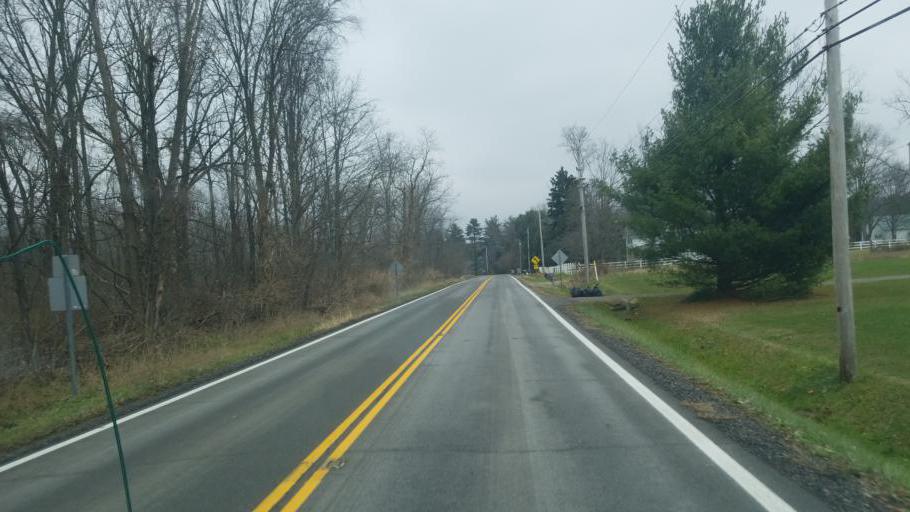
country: US
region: Ohio
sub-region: Cuyahoga County
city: North Royalton
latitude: 41.2408
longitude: -81.7258
